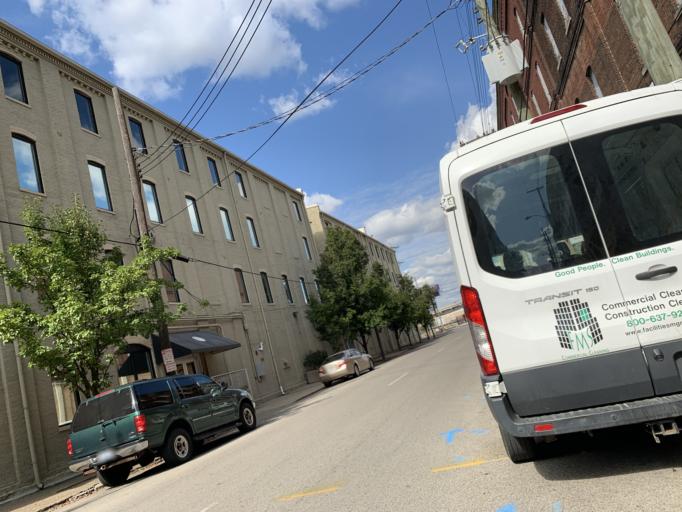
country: US
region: Kentucky
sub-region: Jefferson County
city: Louisville
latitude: 38.2613
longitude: -85.7742
